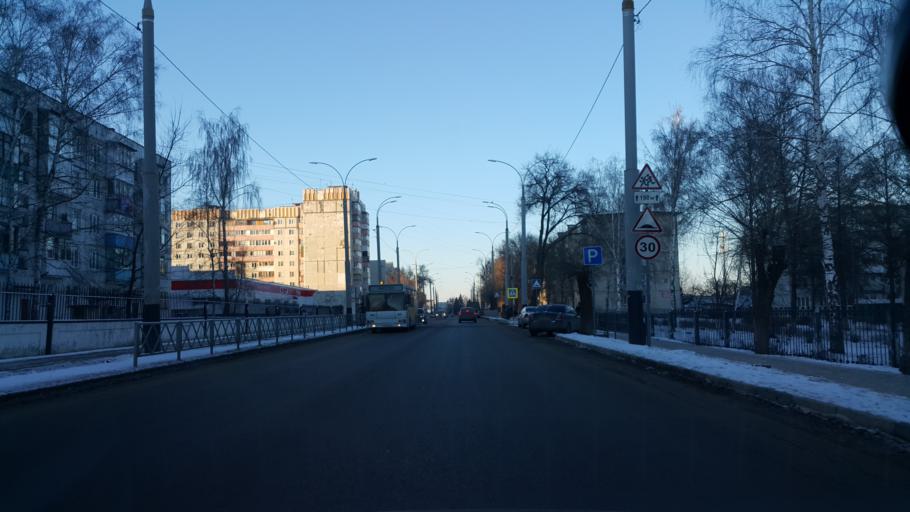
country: RU
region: Tambov
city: Pokrovo-Prigorodnoye
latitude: 52.7063
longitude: 41.3985
